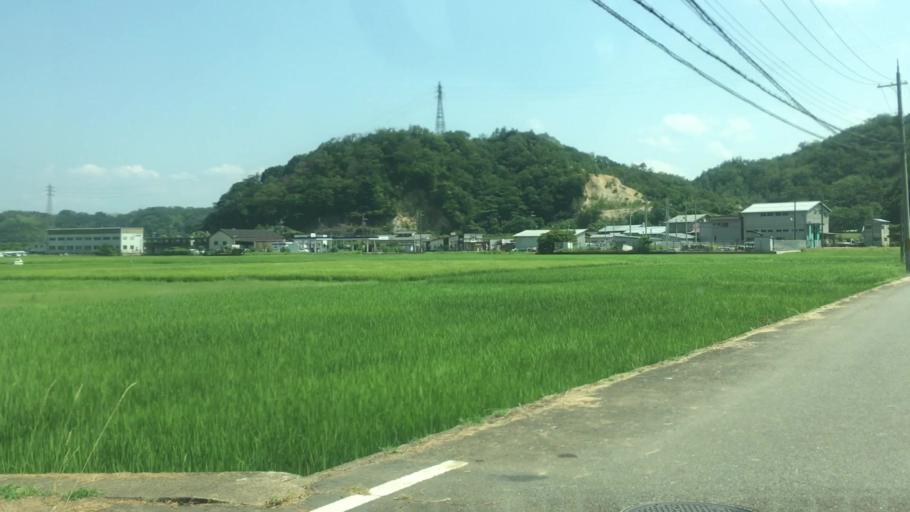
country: JP
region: Hyogo
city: Toyooka
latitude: 35.5672
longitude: 134.7920
